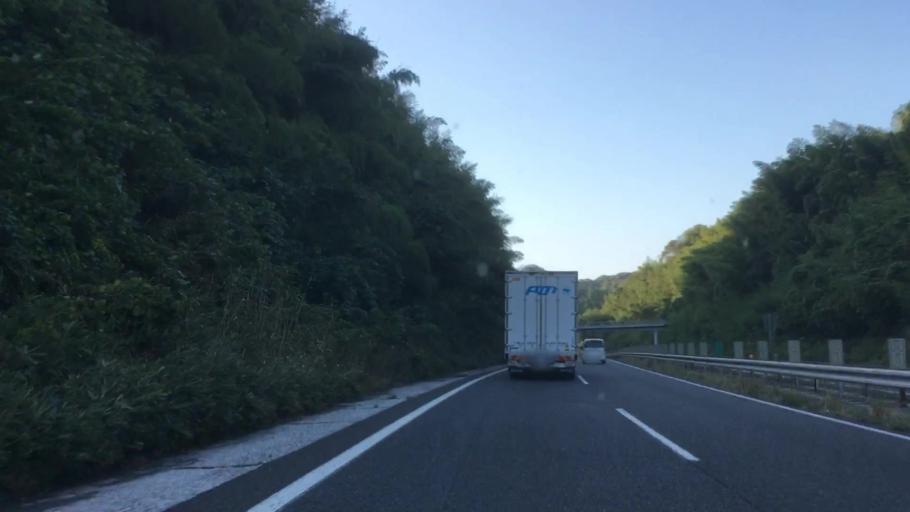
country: JP
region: Yamaguchi
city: Onoda
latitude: 34.1122
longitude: 131.1341
